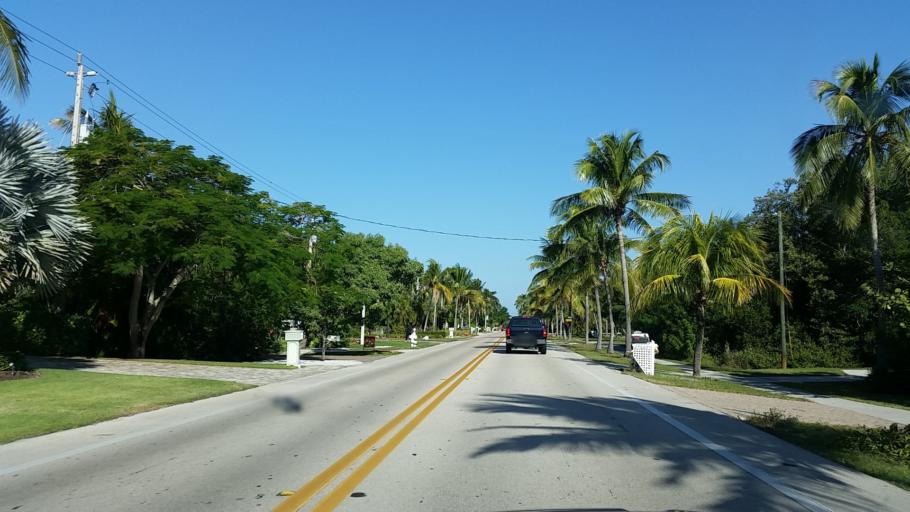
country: US
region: Florida
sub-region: Lee County
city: Bonita Springs
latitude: 26.3365
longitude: -81.8474
